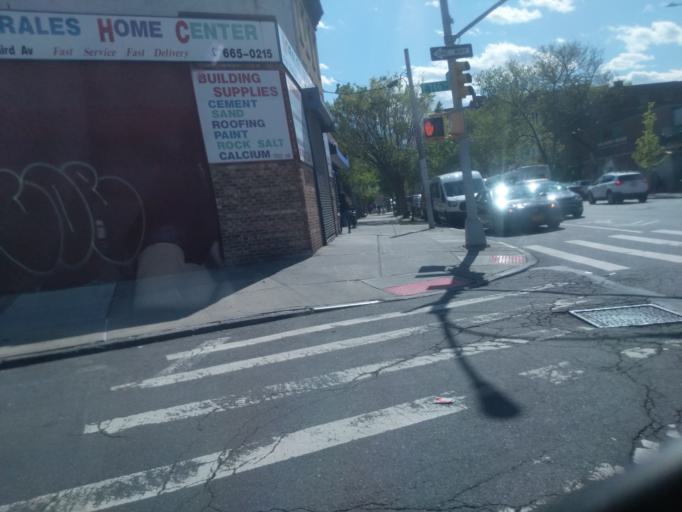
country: US
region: New York
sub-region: New York County
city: Inwood
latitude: 40.8146
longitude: -73.9203
